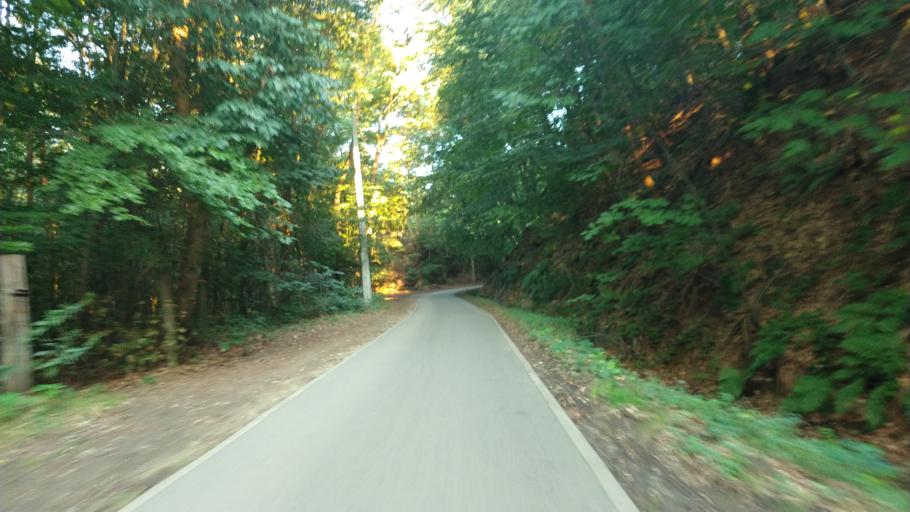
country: BE
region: Flanders
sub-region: Provincie Vlaams-Brabant
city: Holsbeek
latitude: 50.8848
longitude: 4.7774
